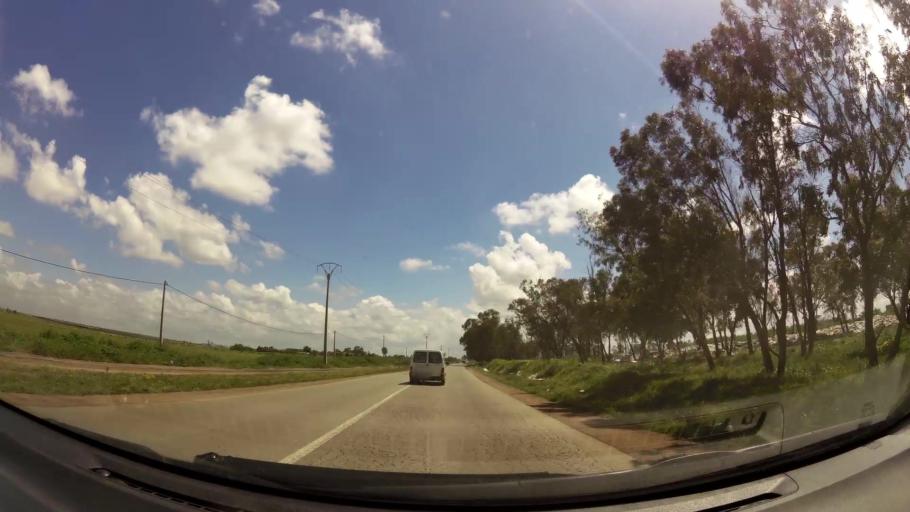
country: MA
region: Grand Casablanca
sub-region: Nouaceur
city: Dar Bouazza
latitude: 33.4182
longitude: -7.8104
